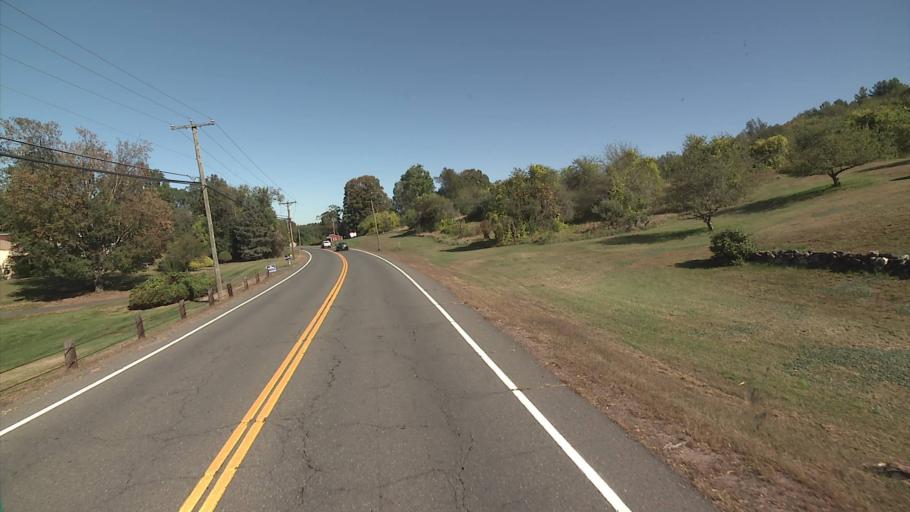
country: US
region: Connecticut
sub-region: Tolland County
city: Somers
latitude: 41.9734
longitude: -72.4436
